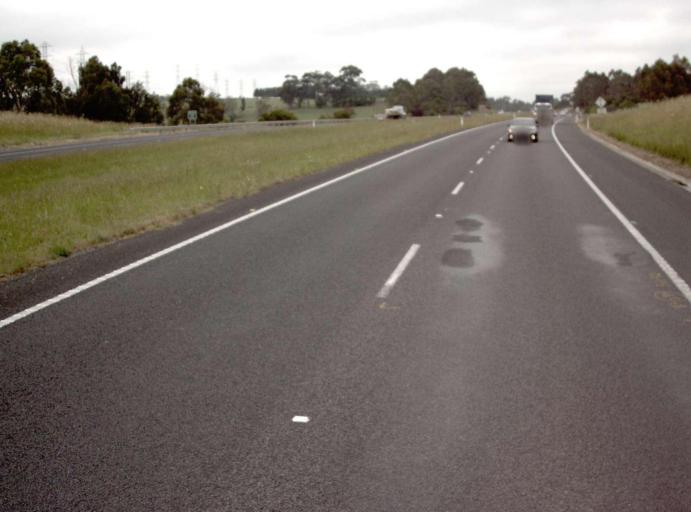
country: AU
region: Victoria
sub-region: Cardinia
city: Bunyip
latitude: -38.0908
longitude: 145.8121
